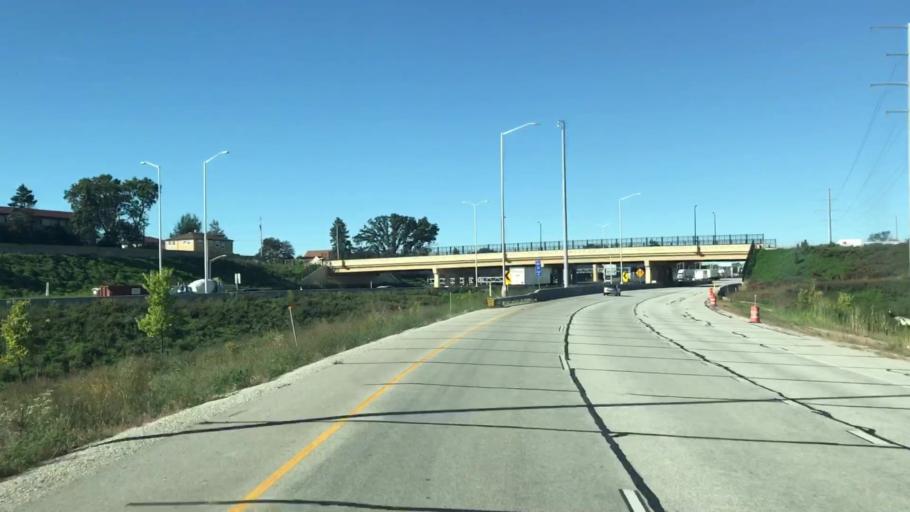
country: US
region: Wisconsin
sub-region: Milwaukee County
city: Saint Francis
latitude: 42.9628
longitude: -87.9367
